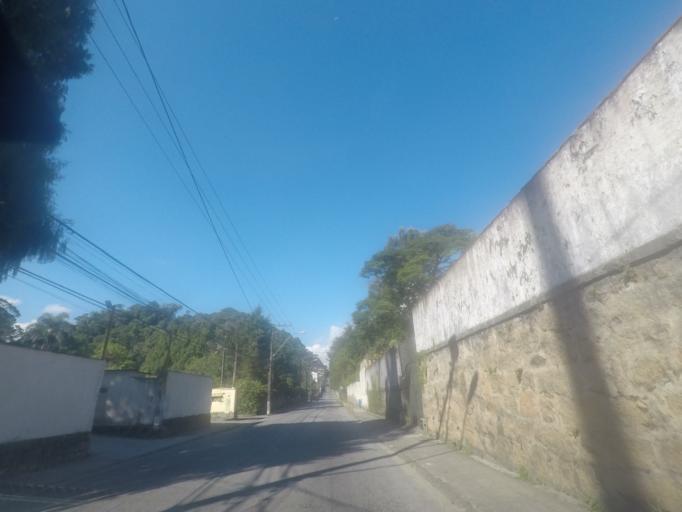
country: BR
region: Rio de Janeiro
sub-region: Petropolis
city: Petropolis
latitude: -22.5334
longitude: -43.1950
